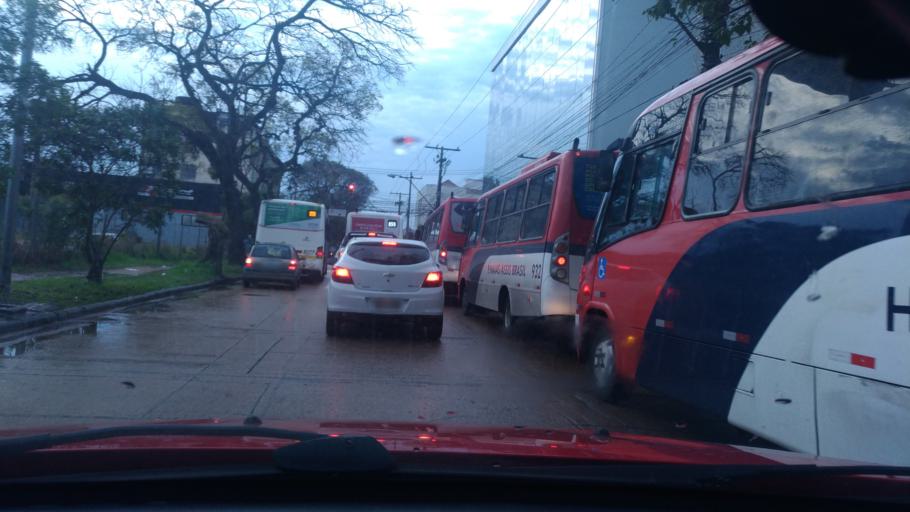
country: BR
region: Rio Grande do Sul
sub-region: Porto Alegre
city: Porto Alegre
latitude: -30.0055
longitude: -51.2001
